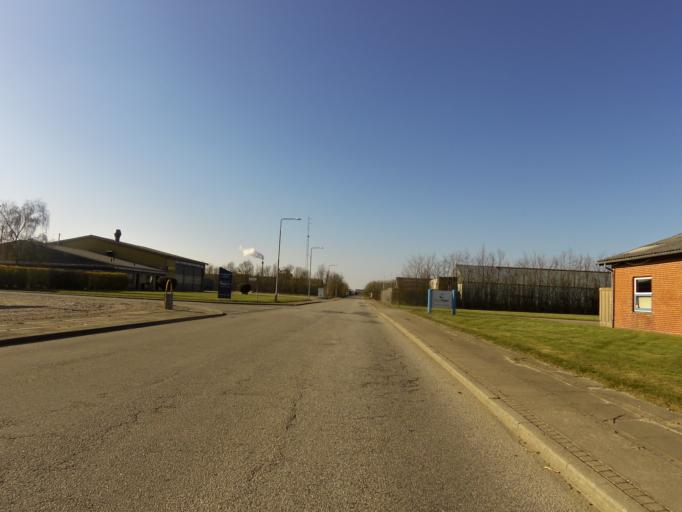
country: DK
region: South Denmark
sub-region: Esbjerg Kommune
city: Ribe
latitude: 55.3537
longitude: 8.7705
